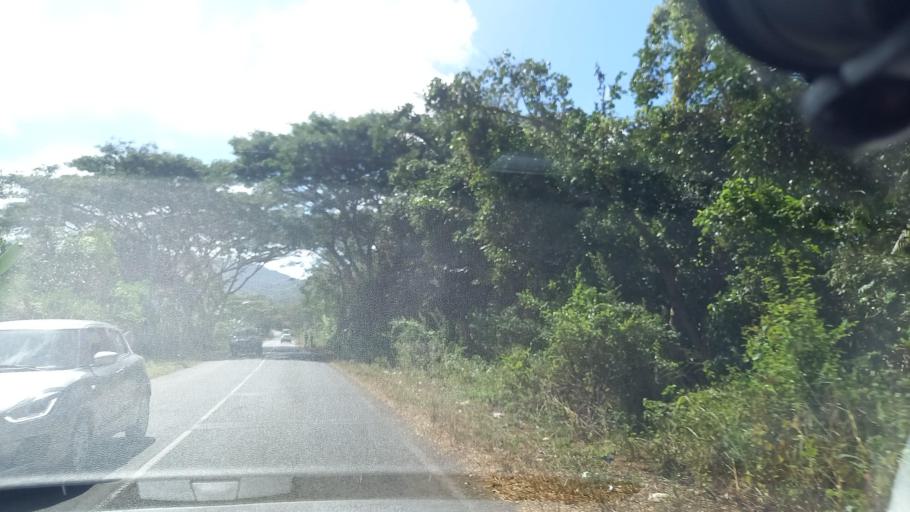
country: YT
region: Chirongui
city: Chirongui
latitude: -12.9172
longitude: 45.1593
